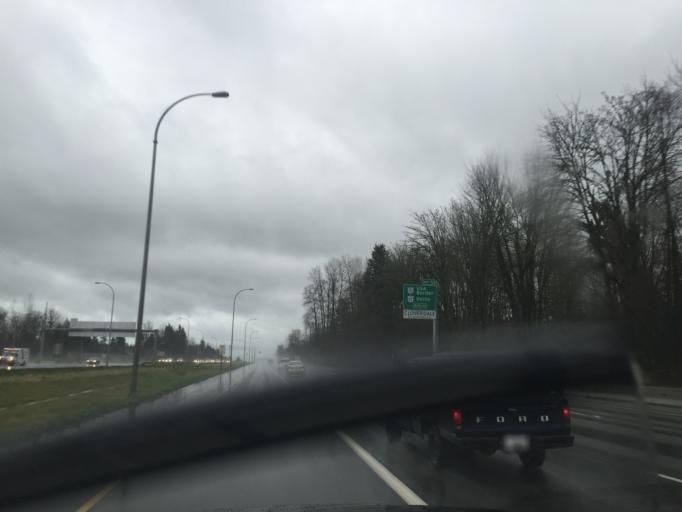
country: CA
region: British Columbia
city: Pitt Meadows
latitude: 49.1858
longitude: -122.7524
